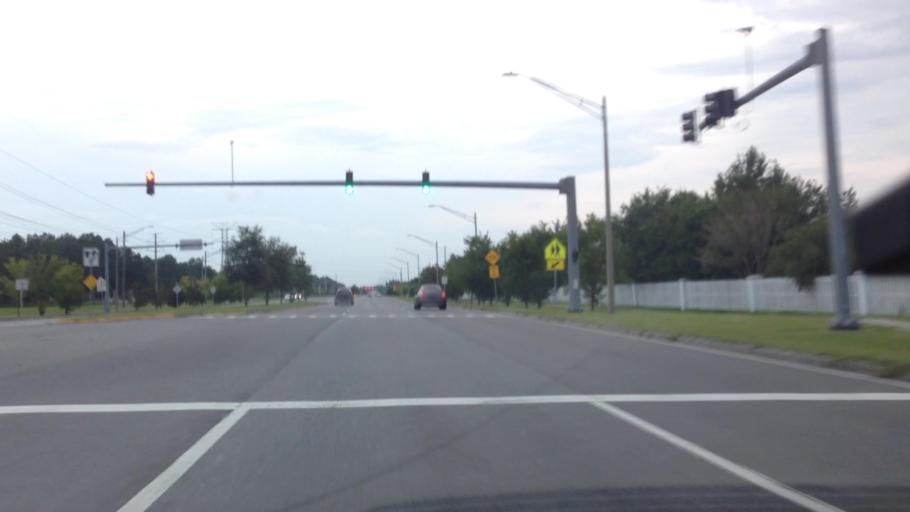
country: US
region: Florida
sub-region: Duval County
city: Neptune Beach
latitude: 30.3046
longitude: -81.4892
